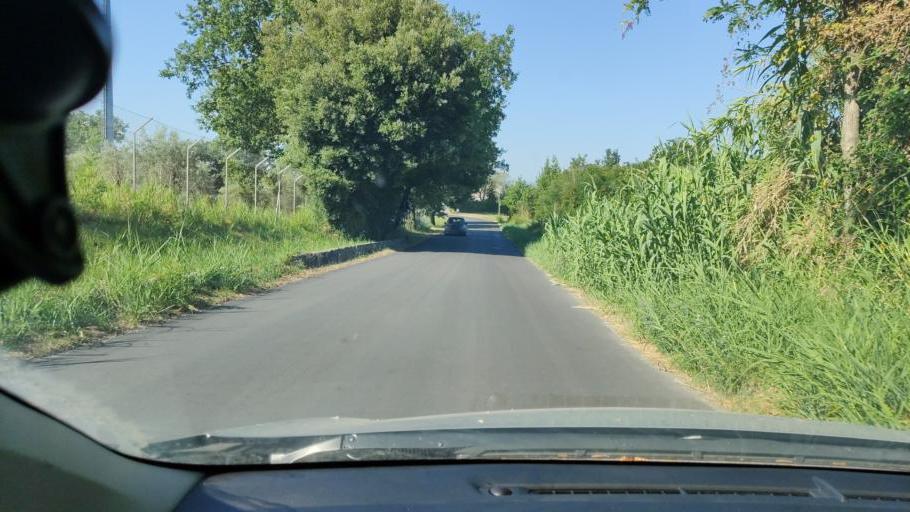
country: IT
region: Umbria
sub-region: Provincia di Terni
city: Fornole
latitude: 42.5358
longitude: 12.4525
